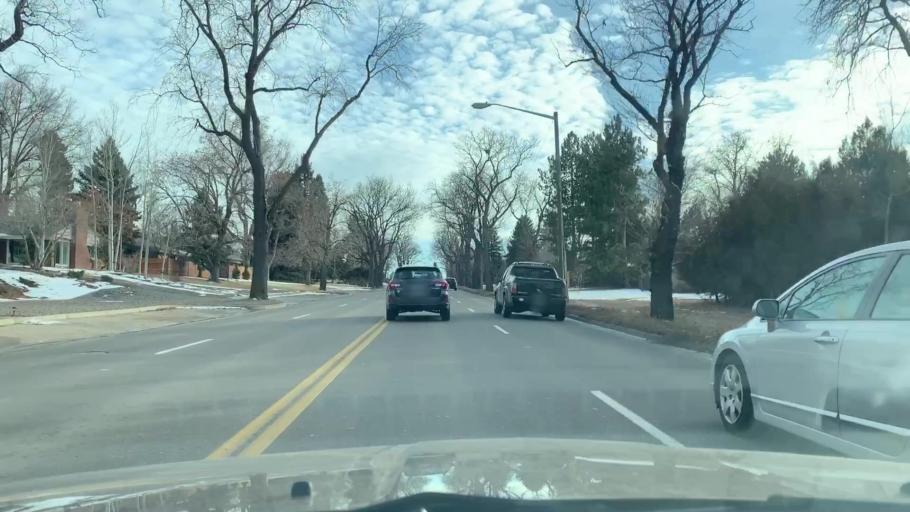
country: US
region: Colorado
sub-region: Arapahoe County
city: Glendale
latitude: 39.7215
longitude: -104.9128
